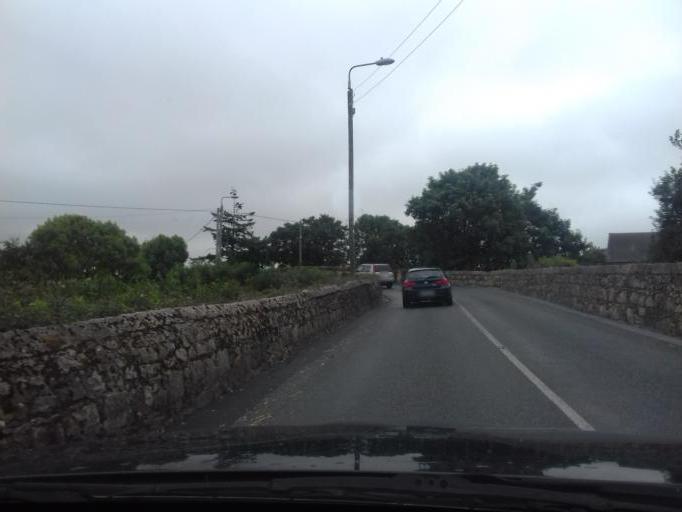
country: IE
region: Leinster
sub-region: County Carlow
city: Bagenalstown
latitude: 52.6968
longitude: -6.9567
